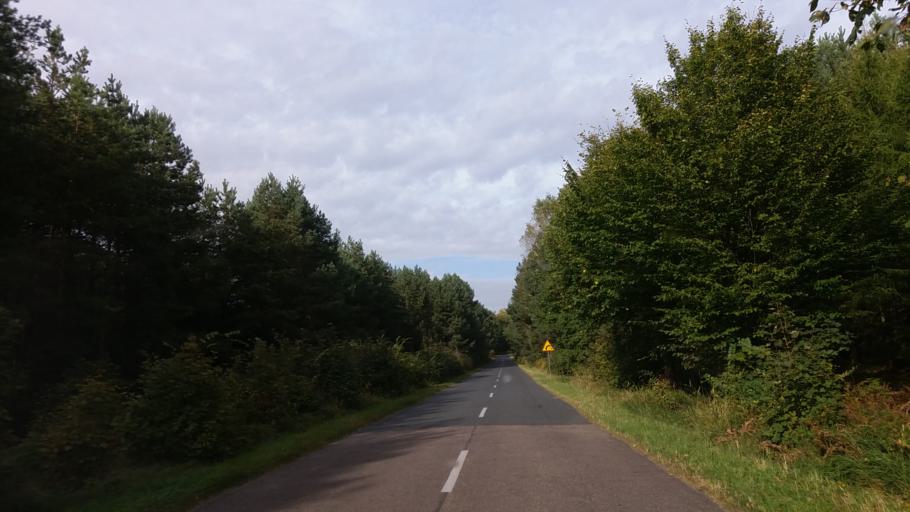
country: PL
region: West Pomeranian Voivodeship
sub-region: Powiat choszczenski
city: Krzecin
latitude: 53.0090
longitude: 15.5016
